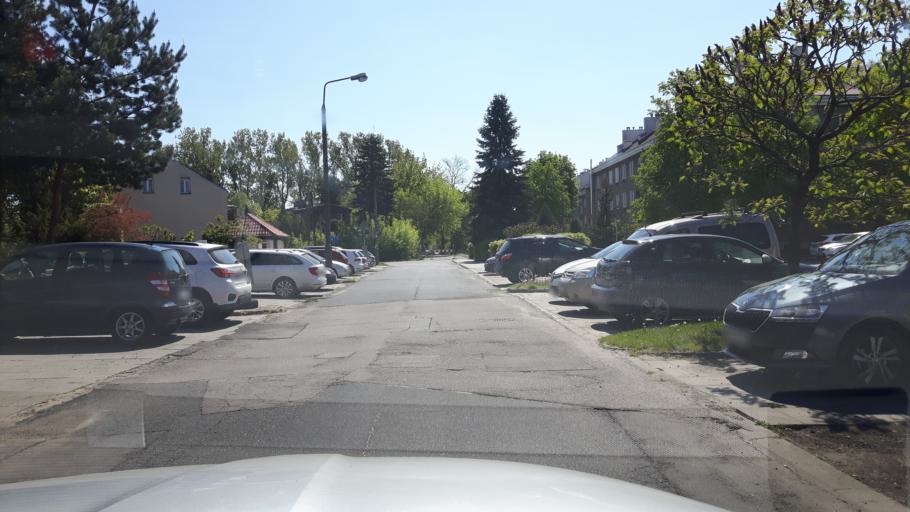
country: PL
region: Masovian Voivodeship
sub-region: Warszawa
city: Rembertow
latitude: 52.2538
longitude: 21.1575
